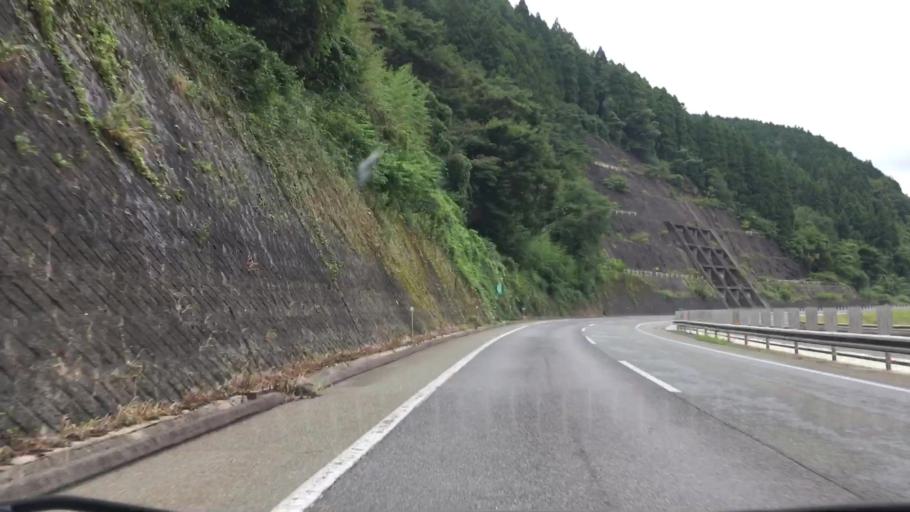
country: JP
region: Hiroshima
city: Shobara
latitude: 34.8971
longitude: 133.2372
